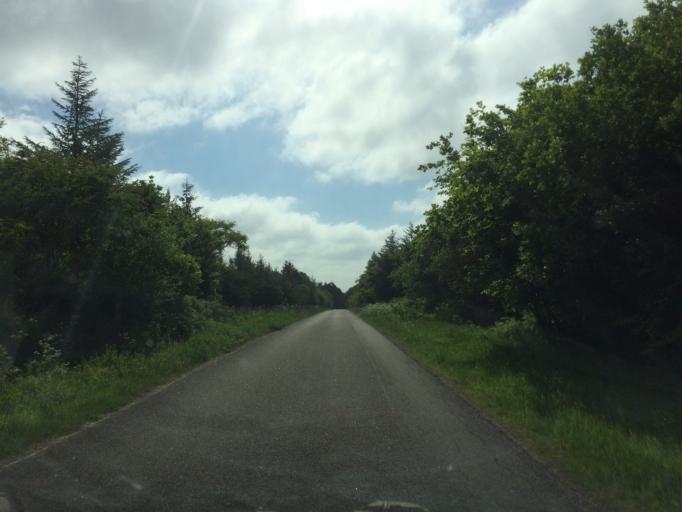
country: DK
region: Central Jutland
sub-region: Holstebro Kommune
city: Ulfborg
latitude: 56.2203
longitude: 8.4462
